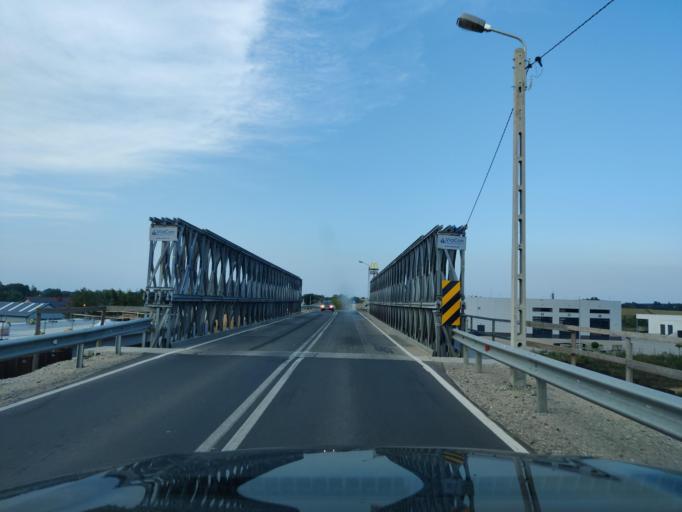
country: PL
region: Masovian Voivodeship
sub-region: Powiat mlawski
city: Mlawa
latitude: 53.0921
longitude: 20.3702
